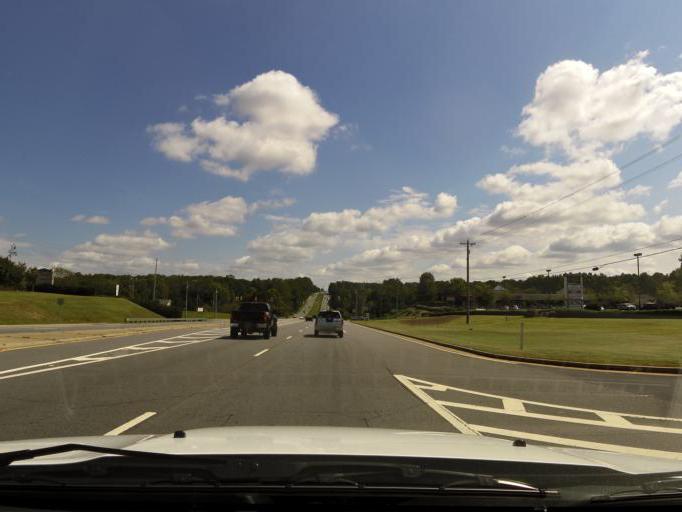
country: US
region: Georgia
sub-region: Cobb County
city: Acworth
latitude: 34.0338
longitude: -84.6734
